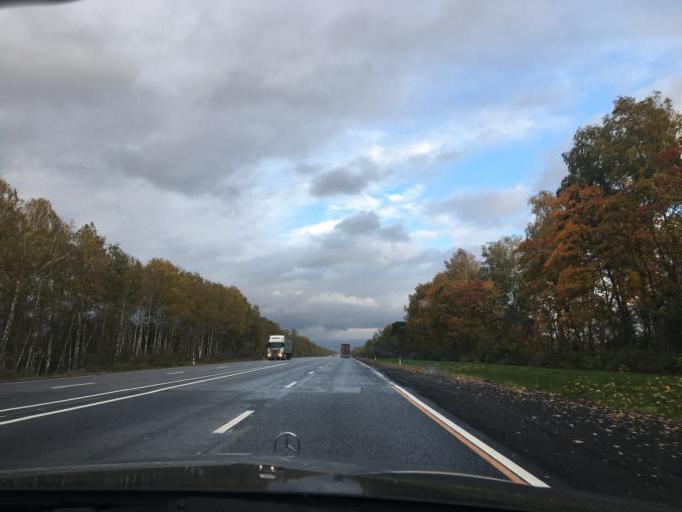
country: RU
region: Smolensk
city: Katyn'
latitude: 54.8495
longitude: 31.8130
